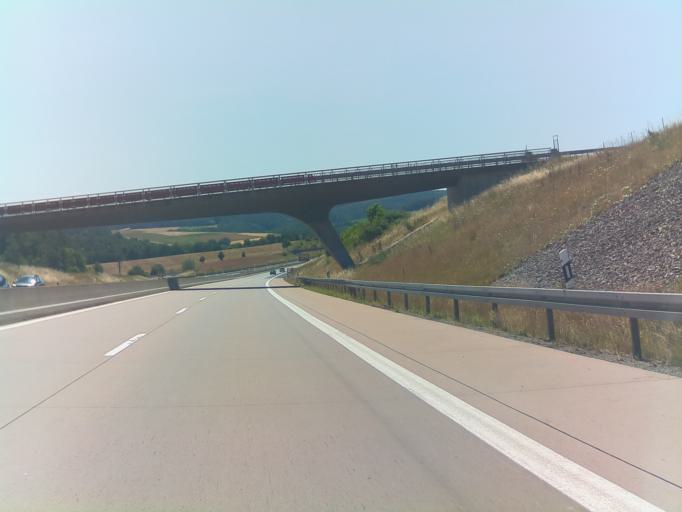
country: DE
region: Bavaria
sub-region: Regierungsbezirk Unterfranken
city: Hollstadt
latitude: 50.3567
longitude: 10.3172
